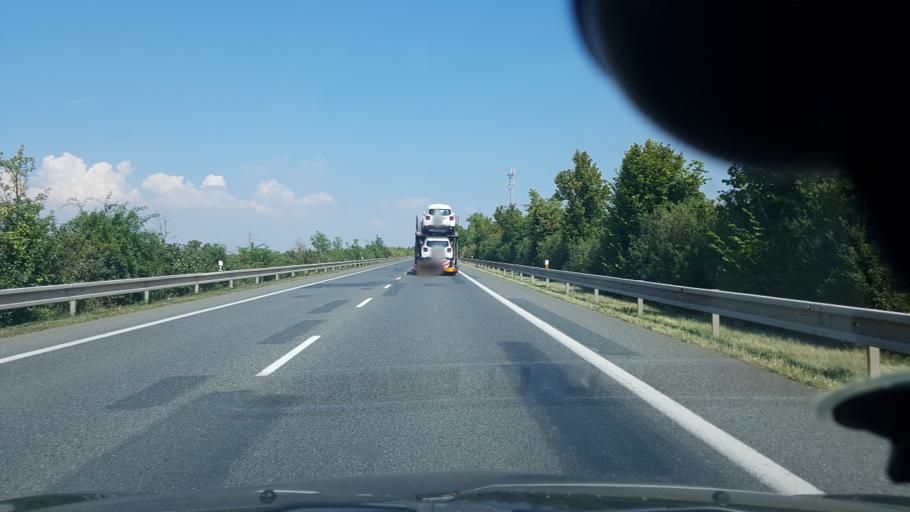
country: CZ
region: South Moravian
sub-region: Okres Breclav
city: Dolni Dunajovice
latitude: 48.8442
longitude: 16.6109
